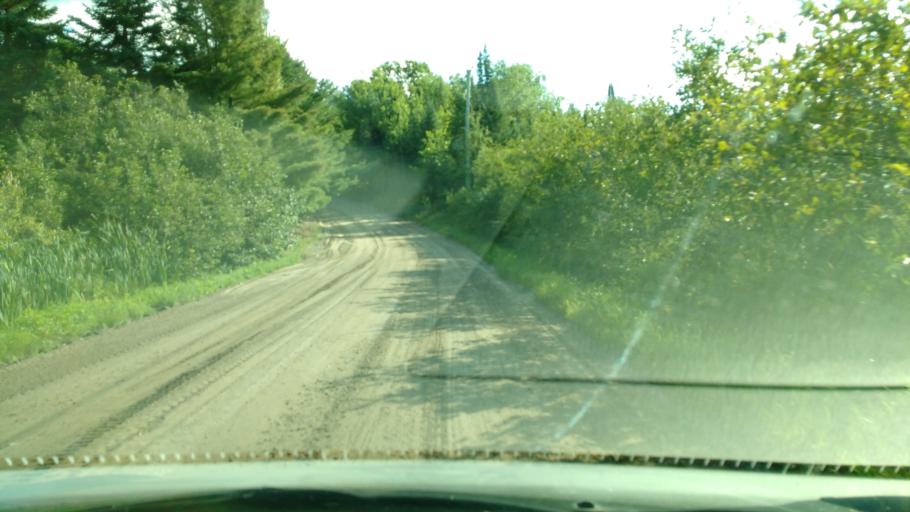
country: CA
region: Ontario
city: Powassan
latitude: 46.1888
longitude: -79.2811
